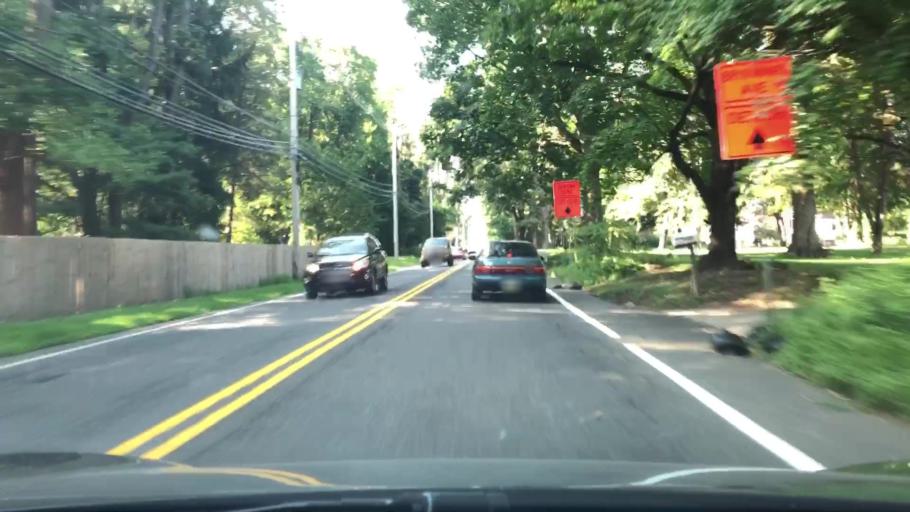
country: US
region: Pennsylvania
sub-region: Delaware County
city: Broomall
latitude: 40.0116
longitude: -75.3655
